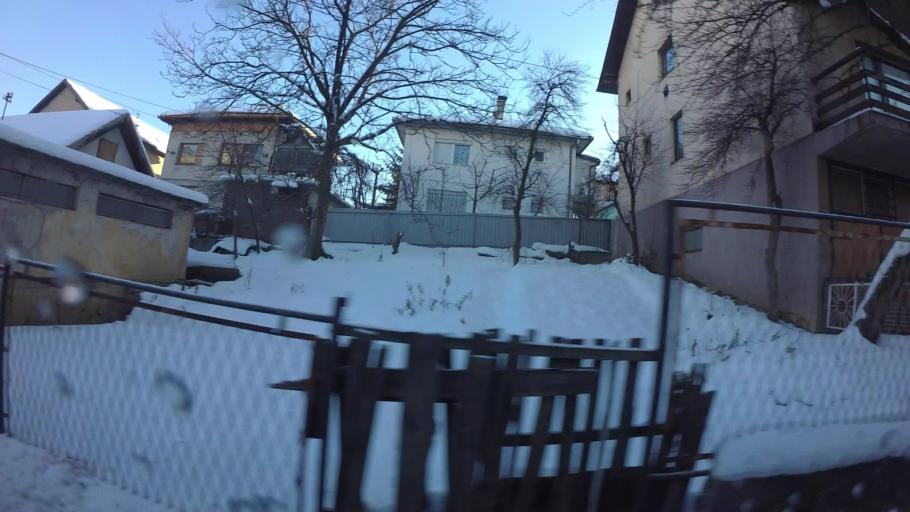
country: BA
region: Federation of Bosnia and Herzegovina
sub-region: Kanton Sarajevo
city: Sarajevo
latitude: 43.8453
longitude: 18.3786
